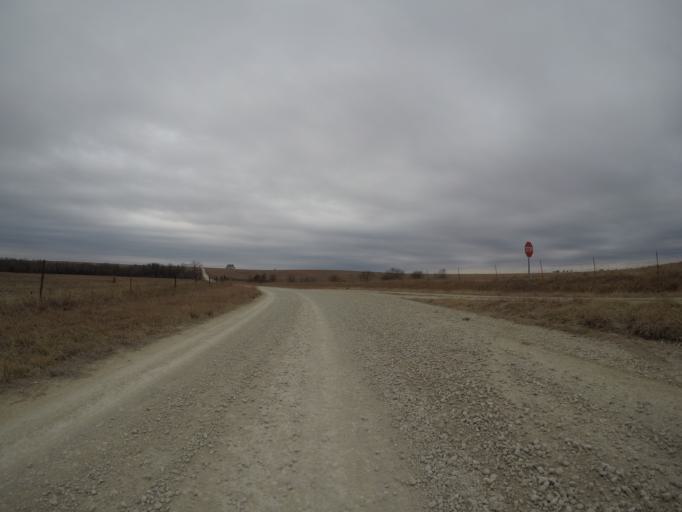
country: US
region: Kansas
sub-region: Wabaunsee County
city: Alma
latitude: 38.7966
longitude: -96.1499
